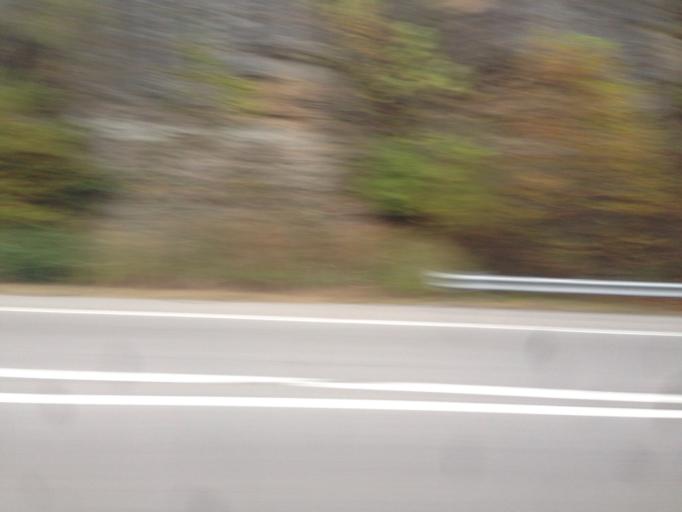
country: US
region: Tennessee
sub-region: Davidson County
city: Nashville
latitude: 36.1412
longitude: -86.7180
